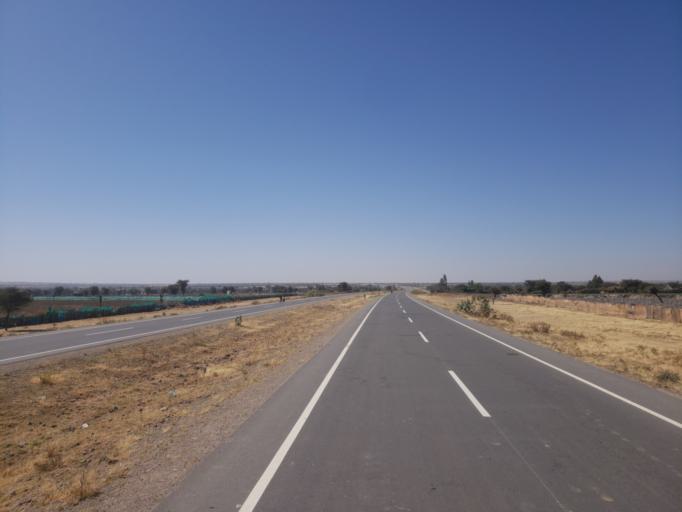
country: ET
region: Oromiya
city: Mojo
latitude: 8.3490
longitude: 38.9811
